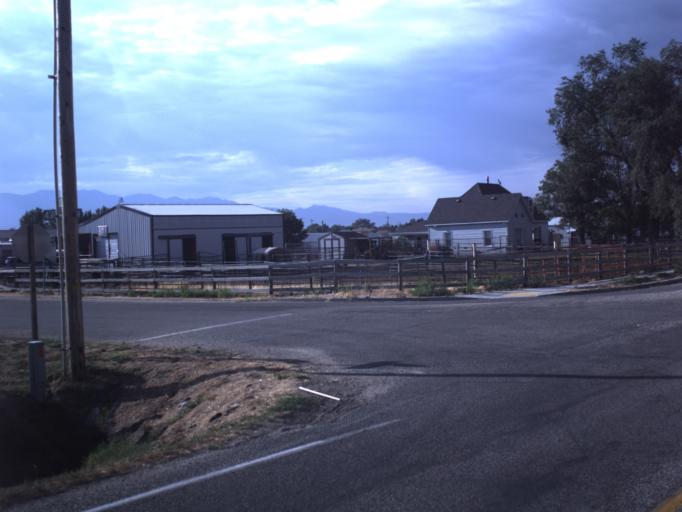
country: US
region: Utah
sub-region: Weber County
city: West Haven
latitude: 41.2233
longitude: -112.0929
